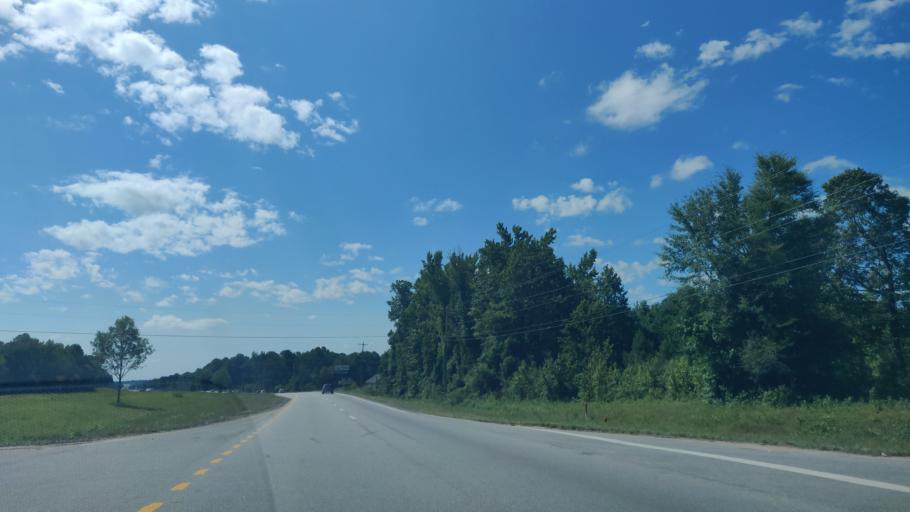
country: US
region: Alabama
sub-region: Lee County
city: Opelika
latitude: 32.6267
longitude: -85.2804
